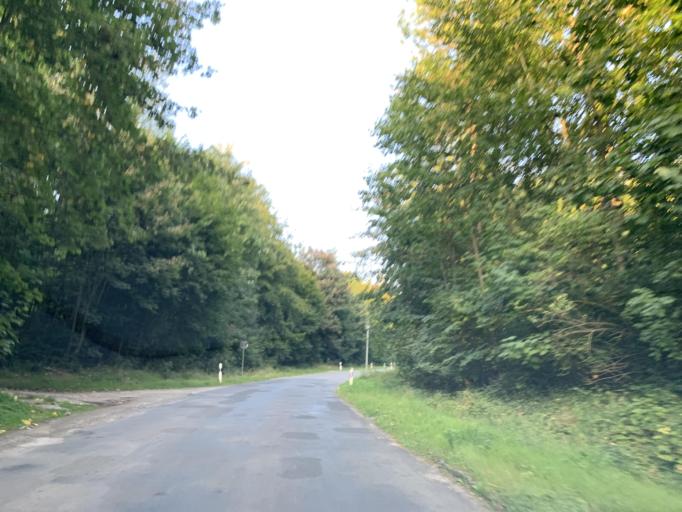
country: DE
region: Mecklenburg-Vorpommern
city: Loitz
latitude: 53.3437
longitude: 13.4272
